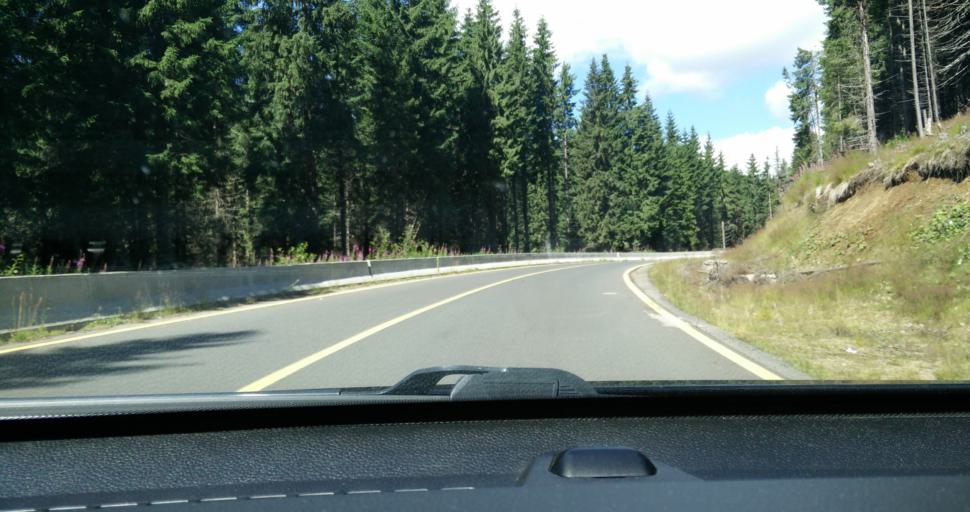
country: RO
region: Hunedoara
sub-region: Oras Petrila
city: Petrila
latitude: 45.4509
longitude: 23.6191
